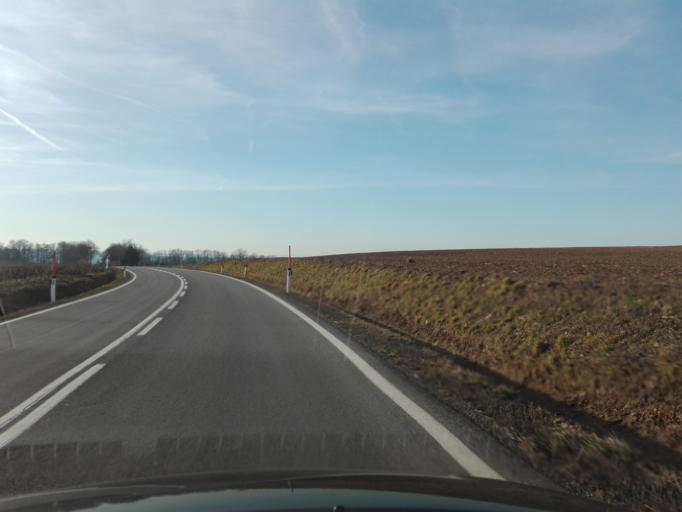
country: AT
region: Lower Austria
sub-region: Politischer Bezirk Amstetten
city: Sankt Valentin
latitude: 48.1876
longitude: 14.5605
